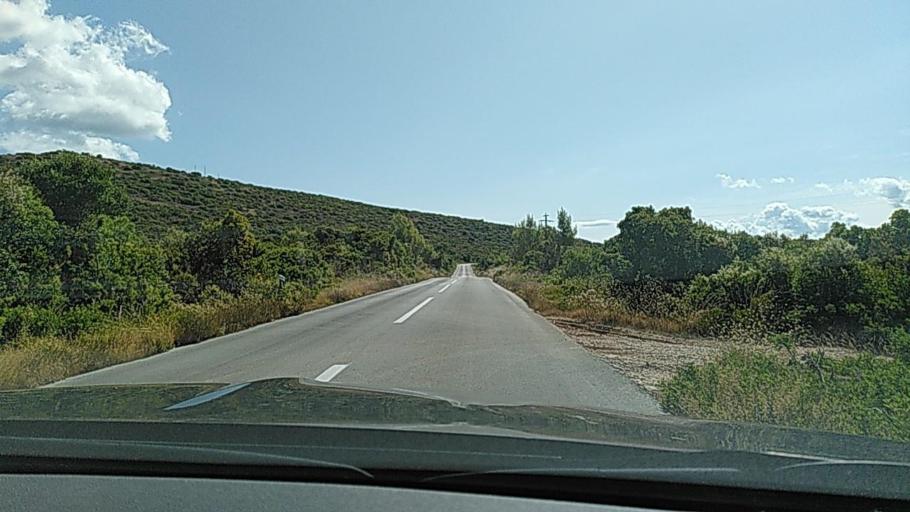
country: HR
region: Splitsko-Dalmatinska
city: Tucepi
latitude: 43.1255
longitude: 17.1046
